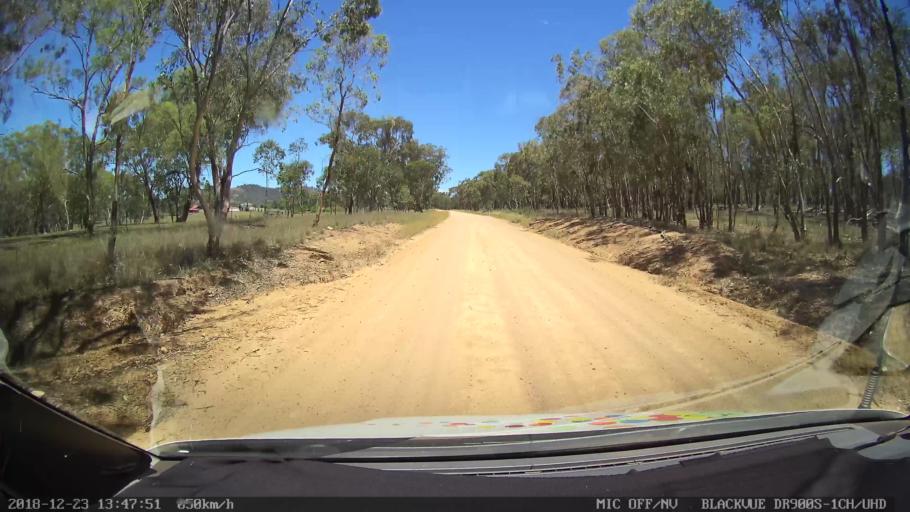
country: AU
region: New South Wales
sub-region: Tamworth Municipality
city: Manilla
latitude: -30.5130
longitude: 151.1153
